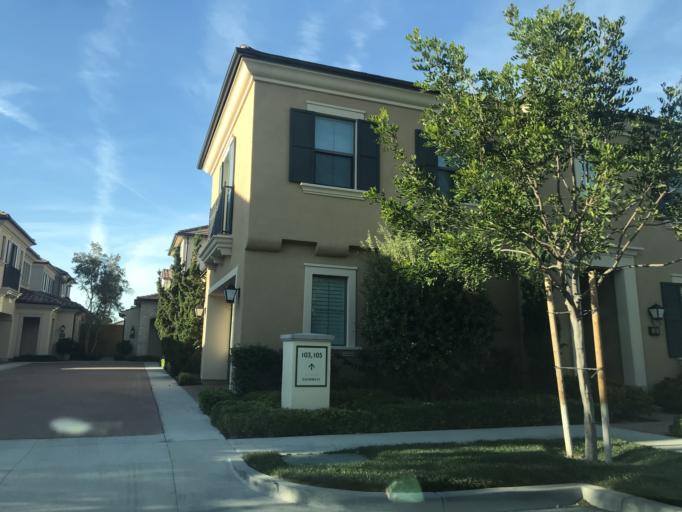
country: US
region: California
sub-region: Orange County
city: North Tustin
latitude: 33.7128
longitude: -117.7528
